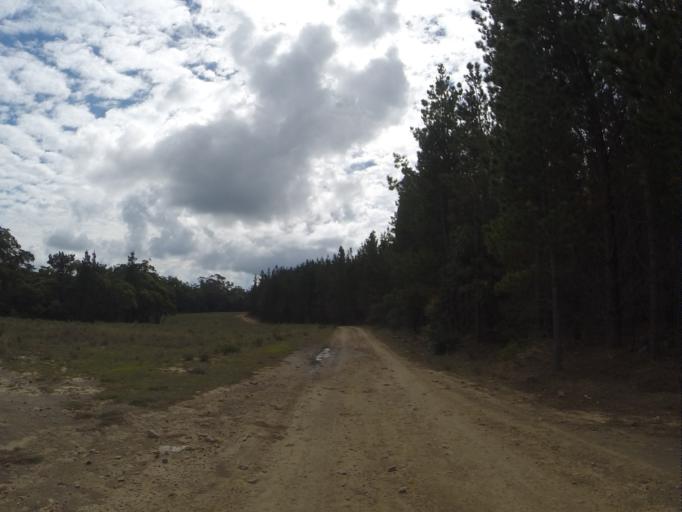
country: AU
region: New South Wales
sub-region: Wingecarribee
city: Moss Vale
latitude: -34.5166
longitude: 150.2275
